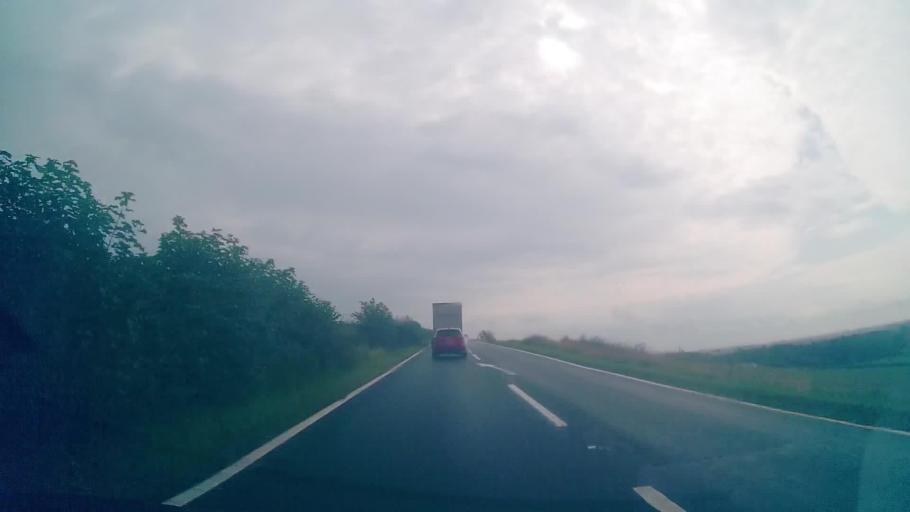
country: GB
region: Scotland
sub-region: Dumfries and Galloway
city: Lochmaben
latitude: 55.0559
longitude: -3.4711
